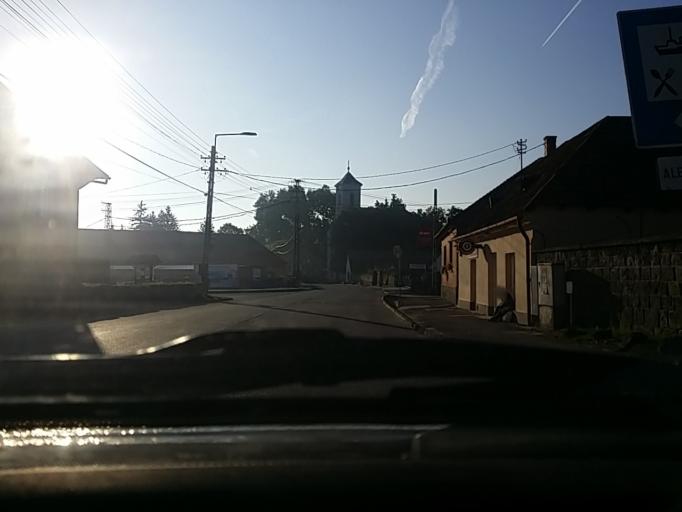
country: HU
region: Komarom-Esztergom
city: Pilismarot
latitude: 47.7852
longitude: 18.8741
